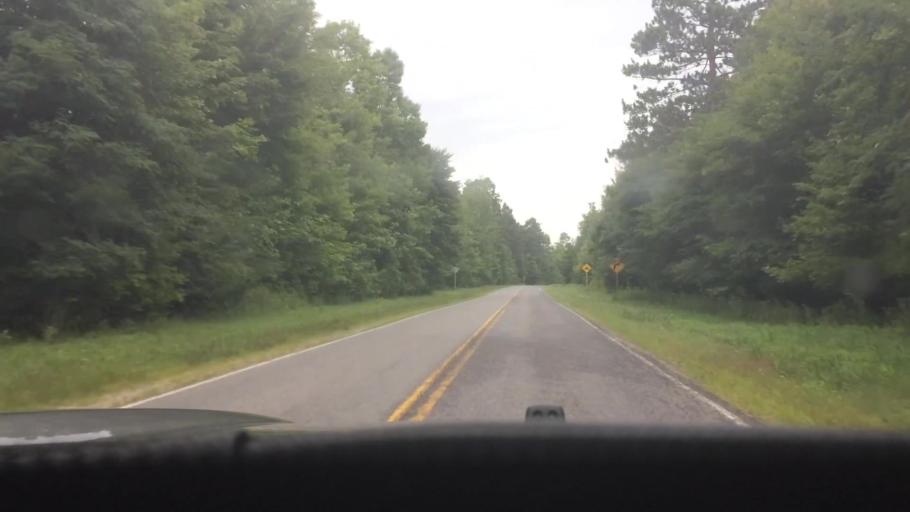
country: US
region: New York
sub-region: St. Lawrence County
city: Hannawa Falls
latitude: 44.6051
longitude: -74.8844
